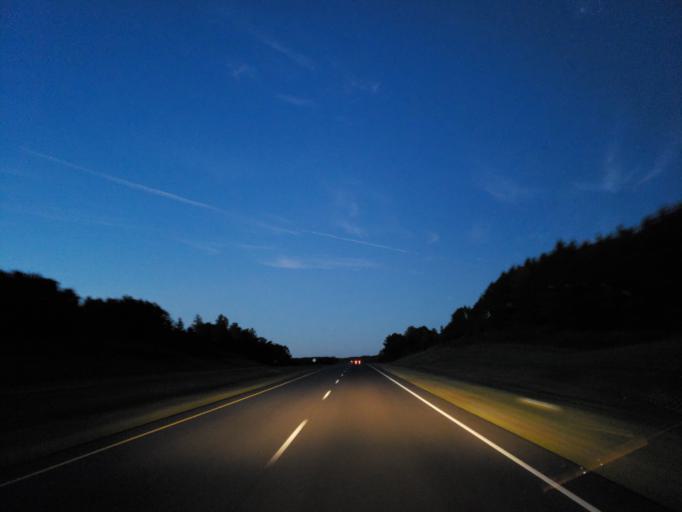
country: US
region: Mississippi
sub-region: Clarke County
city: Quitman
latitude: 32.0264
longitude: -88.6830
